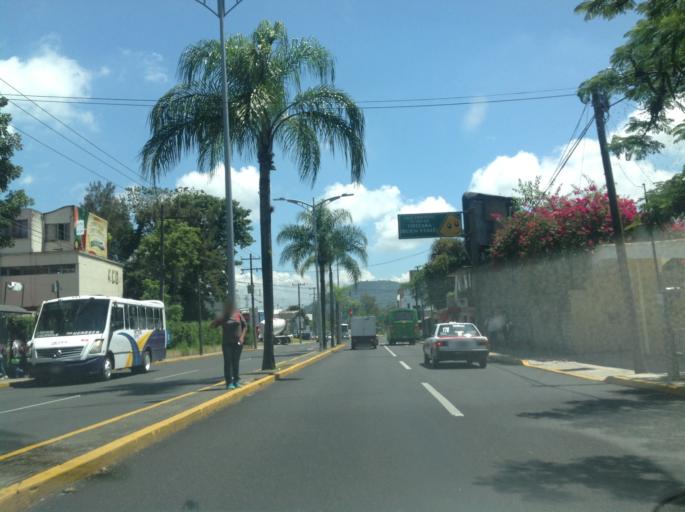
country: MX
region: Veracruz
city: Ixtac Zoquitlan
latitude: 18.8572
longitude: -97.0727
